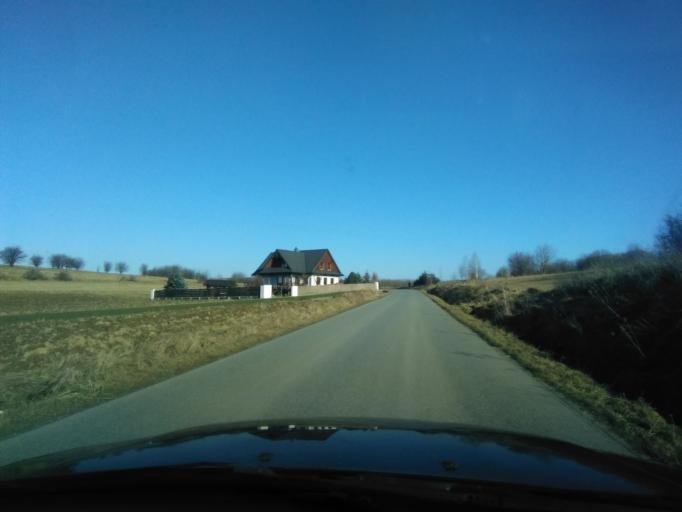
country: PL
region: Subcarpathian Voivodeship
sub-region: Powiat krosnienski
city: Rymanow
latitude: 49.5807
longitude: 21.8820
